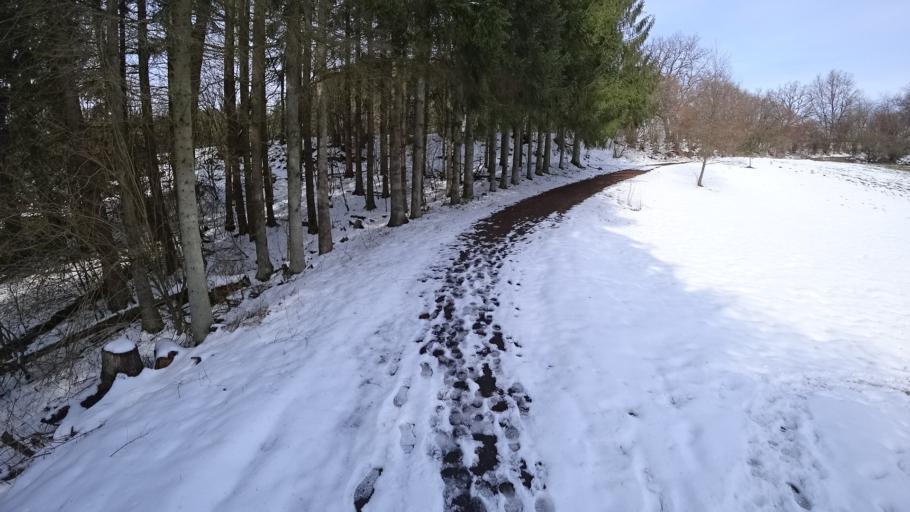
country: DE
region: Rheinland-Pfalz
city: Morlen
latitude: 50.6934
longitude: 7.8792
